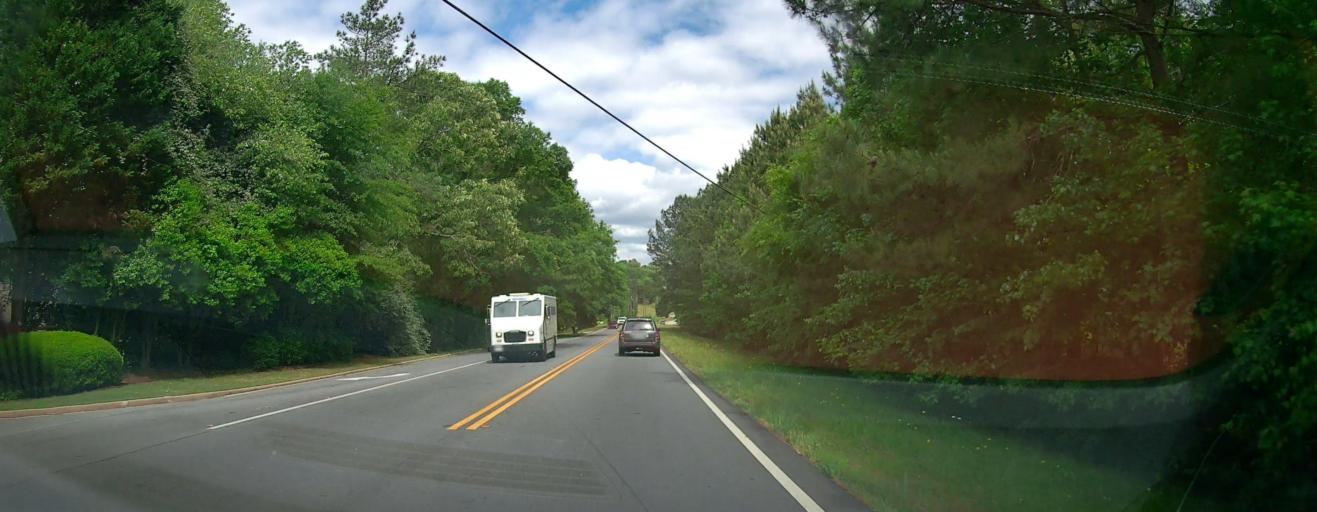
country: US
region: Georgia
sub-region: DeKalb County
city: Pine Mountain
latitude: 33.6209
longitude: -84.0737
